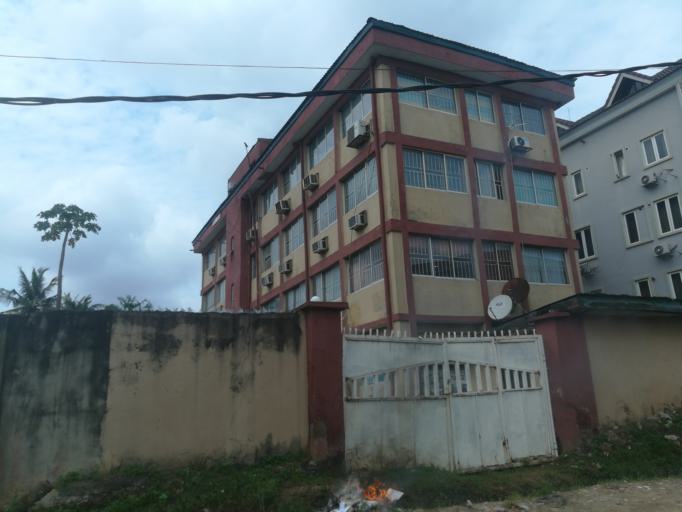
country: NG
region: Lagos
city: Somolu
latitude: 6.5483
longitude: 3.3895
